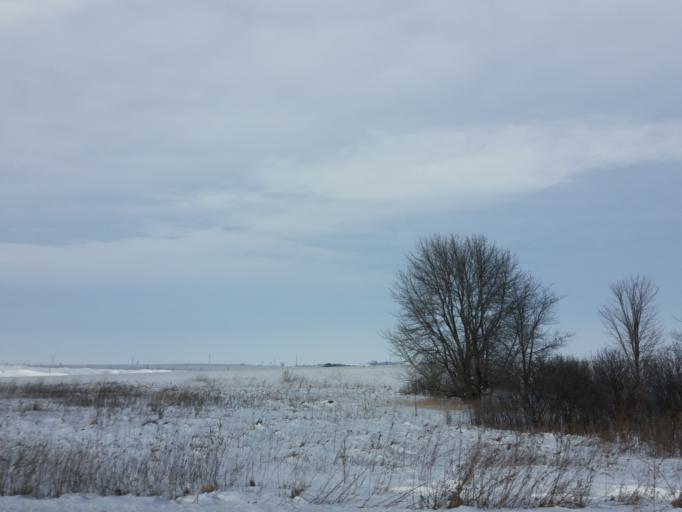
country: US
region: Iowa
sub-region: Delaware County
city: Manchester
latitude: 42.4639
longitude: -91.6485
